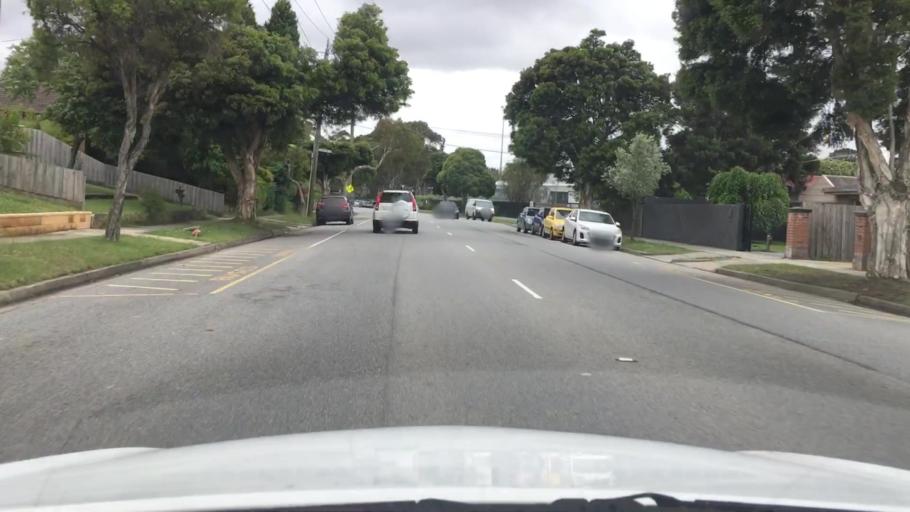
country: AU
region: Victoria
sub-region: Greater Dandenong
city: Noble Park North
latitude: -37.9498
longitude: 145.1918
